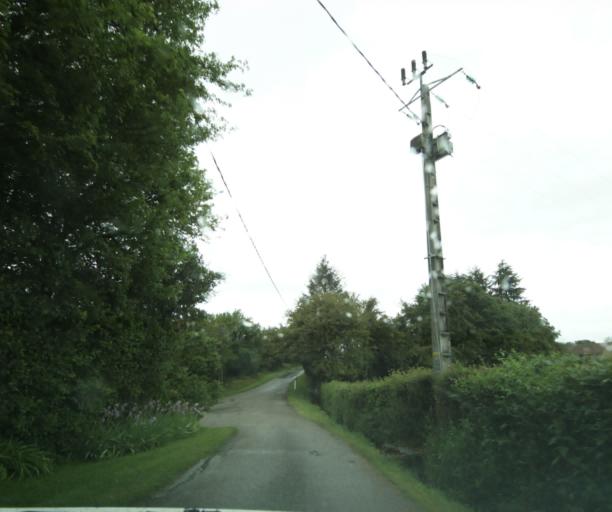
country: FR
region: Bourgogne
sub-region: Departement de Saone-et-Loire
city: Charolles
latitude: 46.5006
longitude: 4.3001
